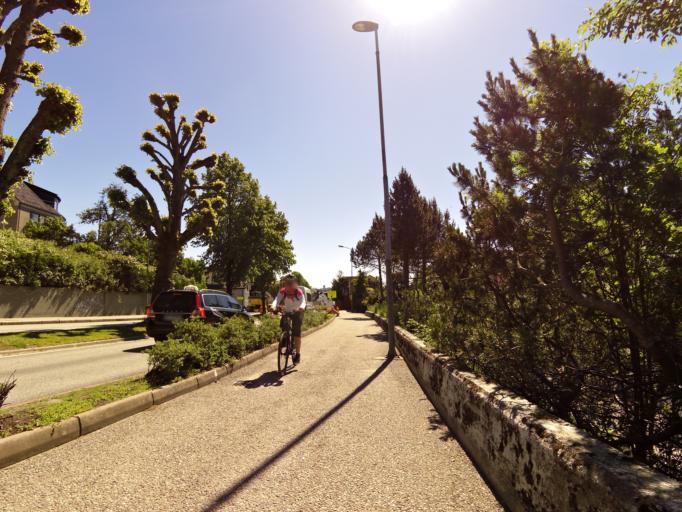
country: NO
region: Vest-Agder
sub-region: Kristiansand
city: Kristiansand
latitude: 58.1546
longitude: 8.0095
